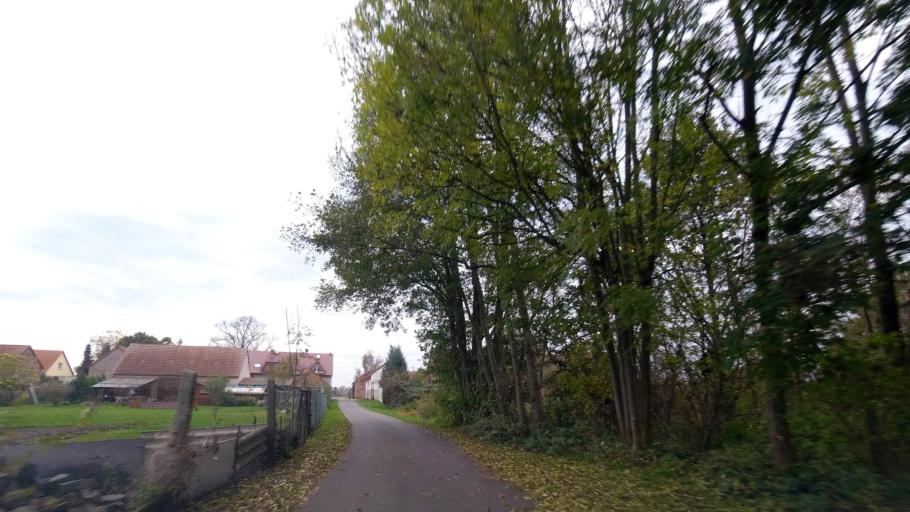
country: DE
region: Brandenburg
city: Borkheide
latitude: 52.1891
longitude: 12.9056
